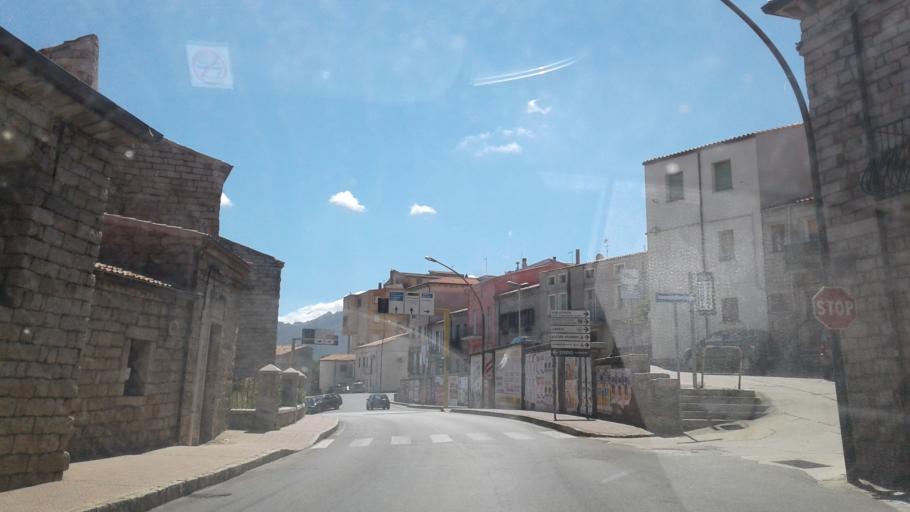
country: IT
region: Sardinia
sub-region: Provincia di Olbia-Tempio
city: Tempio Pausania
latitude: 40.9021
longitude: 9.1059
